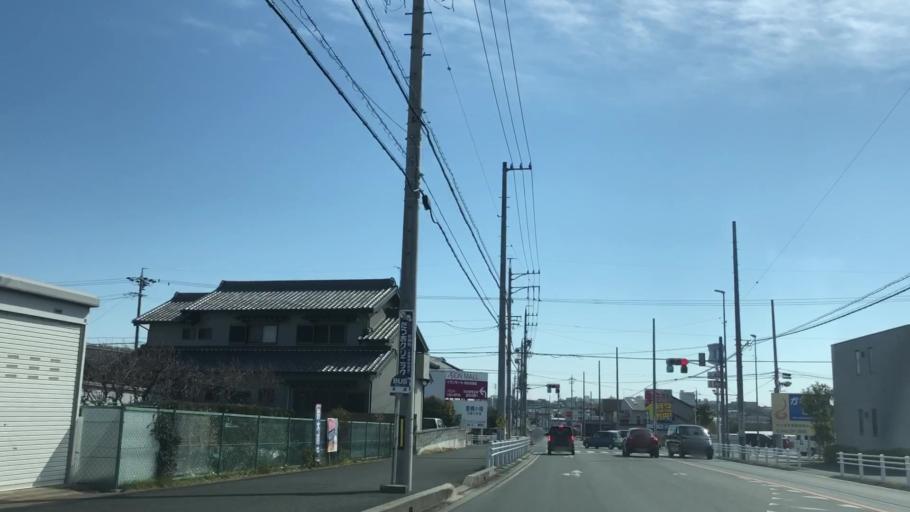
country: JP
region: Aichi
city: Toyohashi
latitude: 34.7194
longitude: 137.4046
